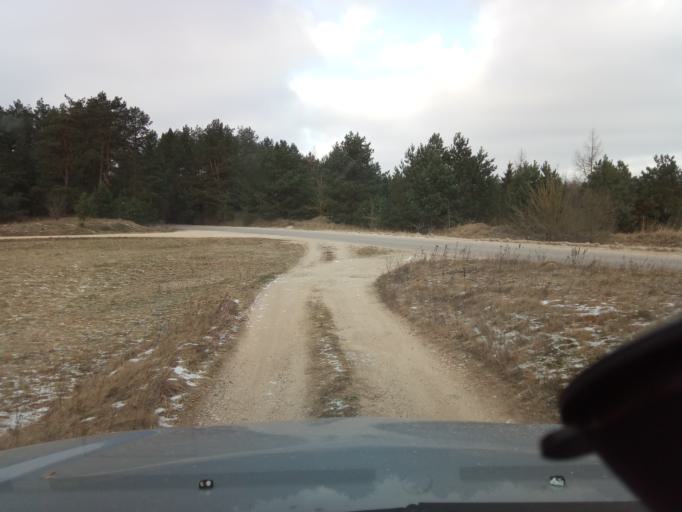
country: LT
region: Alytaus apskritis
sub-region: Alytaus rajonas
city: Daugai
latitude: 54.3337
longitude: 24.2879
